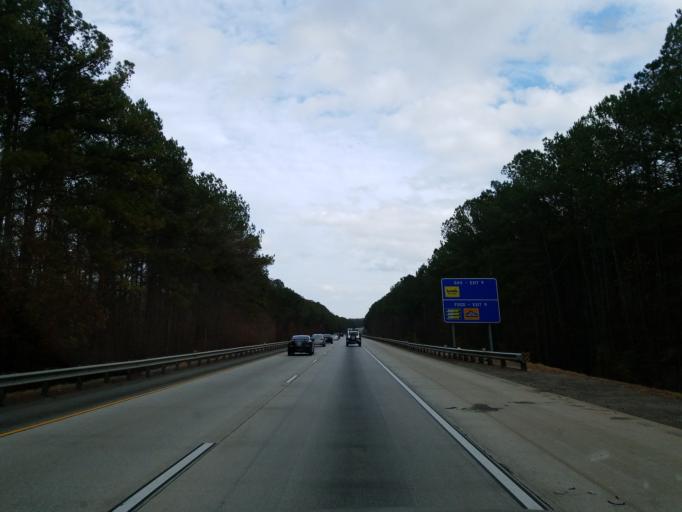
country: US
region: Georgia
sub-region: Carroll County
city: Mount Zion
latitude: 33.6885
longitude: -85.2144
